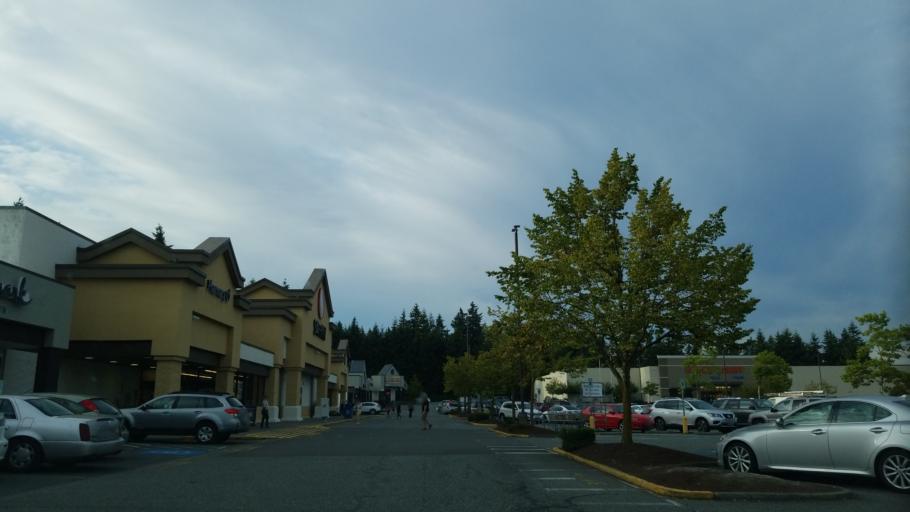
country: US
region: Washington
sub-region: Snohomish County
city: Lynnwood
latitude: 47.8218
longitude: -122.3163
